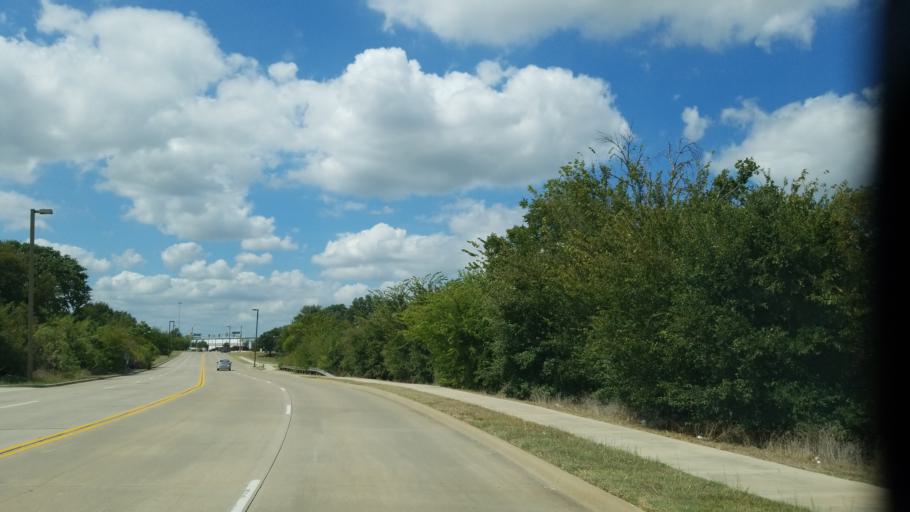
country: US
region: Texas
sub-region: Tarrant County
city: Grapevine
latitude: 32.9050
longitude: -97.0913
